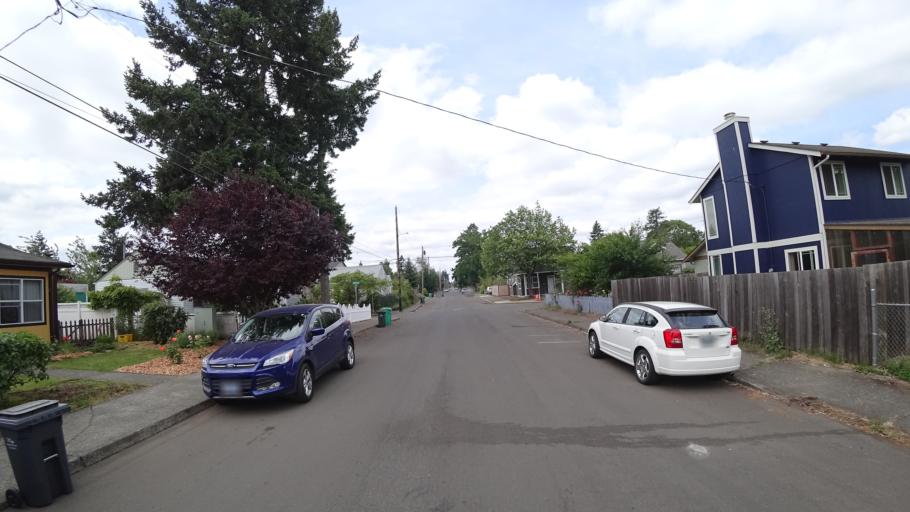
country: US
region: Oregon
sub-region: Multnomah County
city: Lents
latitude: 45.4774
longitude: -122.5899
